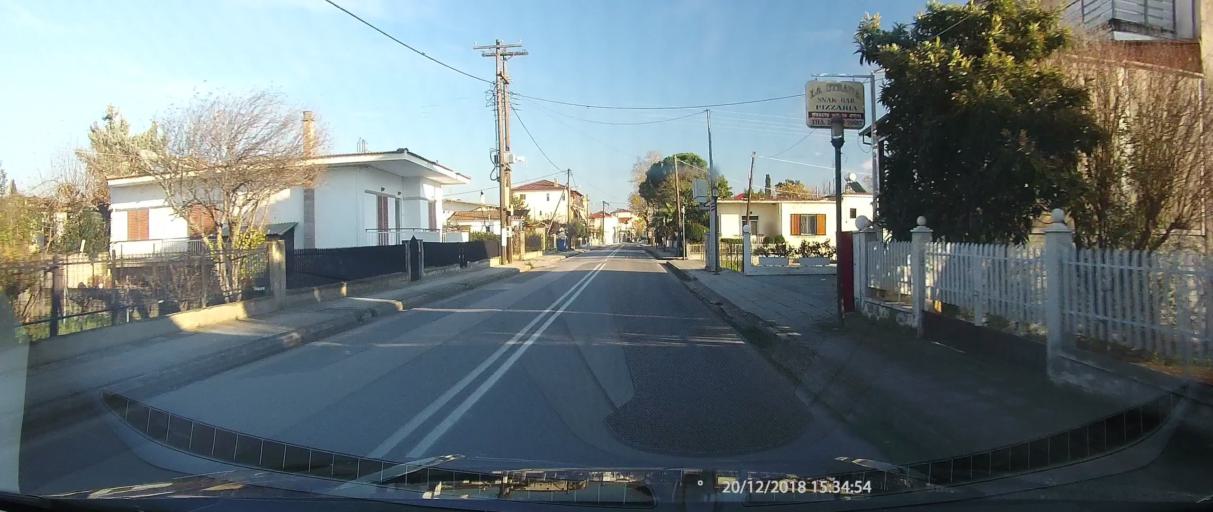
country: GR
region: Central Greece
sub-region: Nomos Fthiotidos
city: Lianokladhion
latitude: 38.9174
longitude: 22.2997
